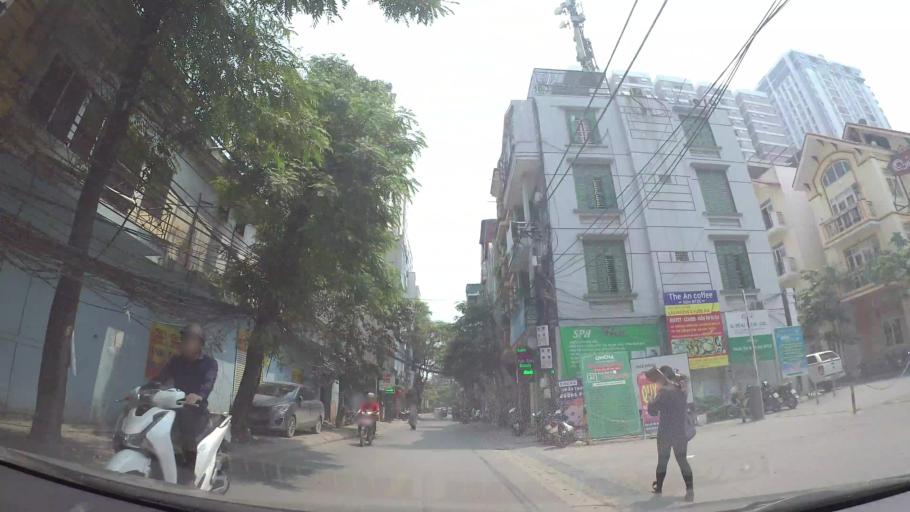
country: VN
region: Ha Noi
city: Thanh Xuan
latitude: 20.9985
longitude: 105.8059
